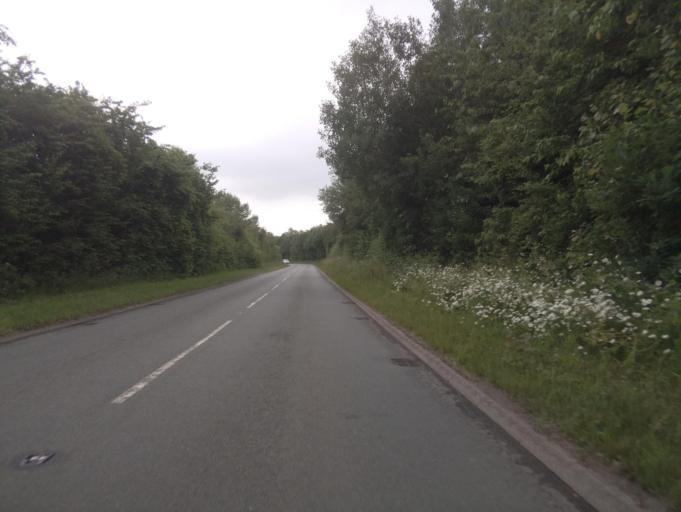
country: GB
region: England
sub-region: Derbyshire
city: Rodsley
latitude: 52.8812
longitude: -1.7070
